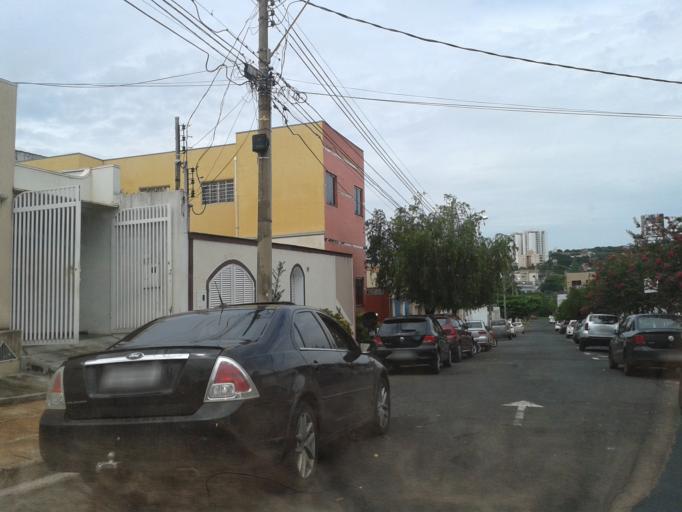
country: BR
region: Minas Gerais
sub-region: Uberlandia
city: Uberlandia
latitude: -18.9251
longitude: -48.2930
